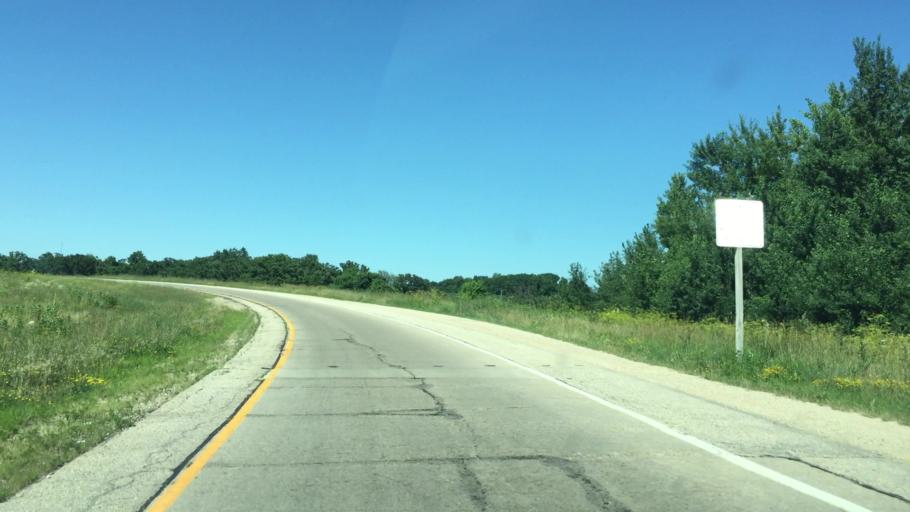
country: US
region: Wisconsin
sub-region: Dane County
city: Verona
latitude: 42.9753
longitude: -89.5124
